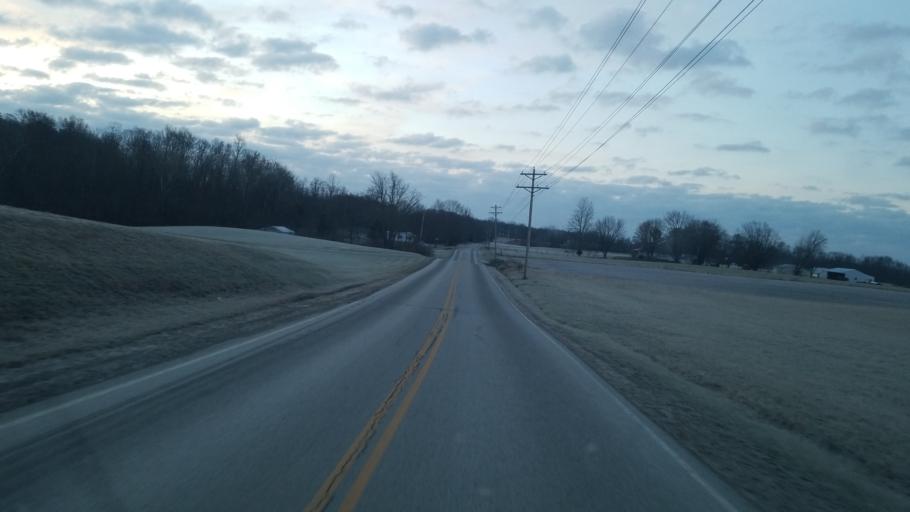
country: US
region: Ohio
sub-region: Highland County
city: Leesburg
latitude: 39.2615
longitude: -83.4744
